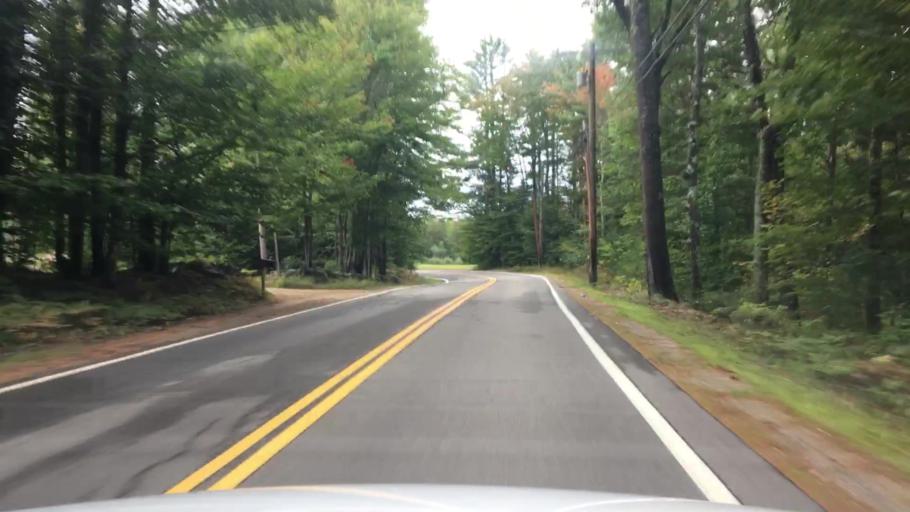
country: US
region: New Hampshire
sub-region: Carroll County
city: Effingham
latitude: 43.7351
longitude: -71.0068
